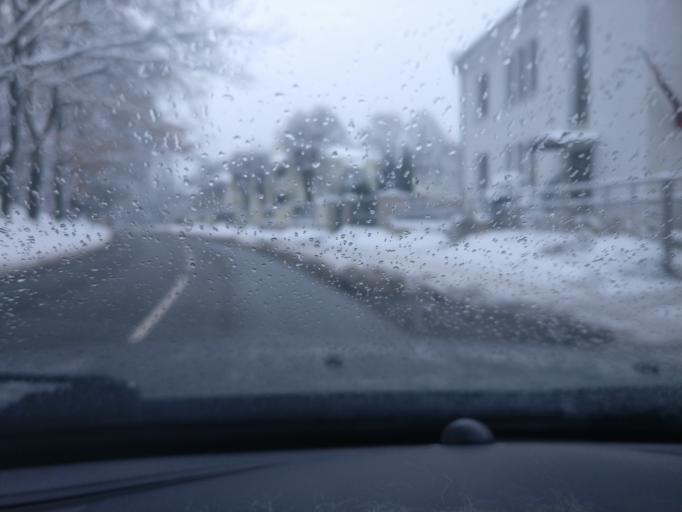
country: LV
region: Riga
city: Riga
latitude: 56.9330
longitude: 24.0797
